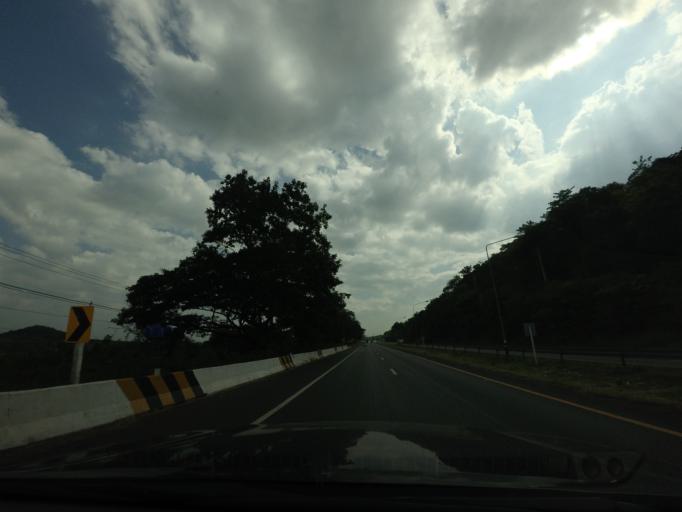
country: TH
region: Lop Buri
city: Chai Badan
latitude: 15.2961
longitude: 101.1293
